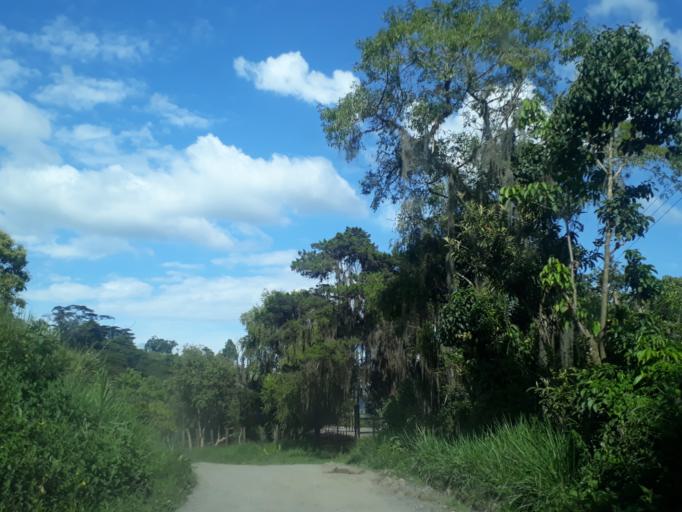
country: CO
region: Santander
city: Velez
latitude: 6.0516
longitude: -73.6511
